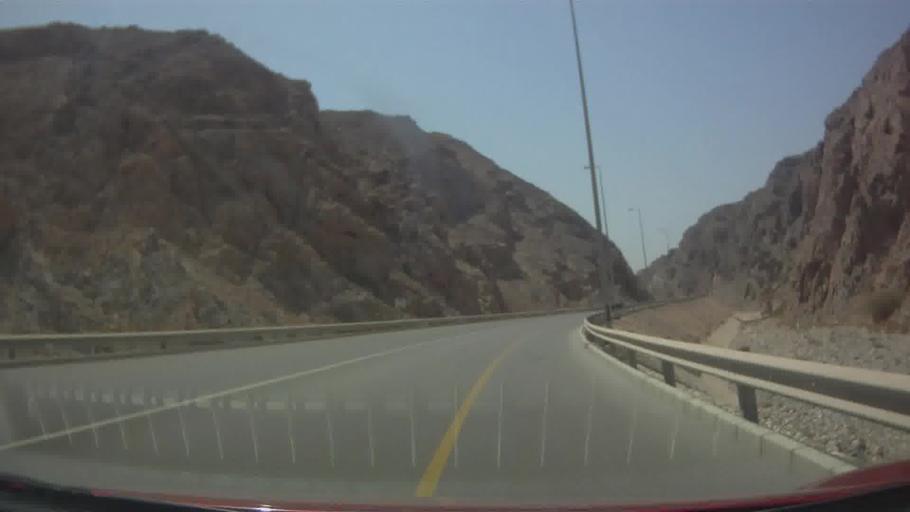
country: OM
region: Muhafazat Masqat
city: Muscat
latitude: 23.5303
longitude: 58.6486
